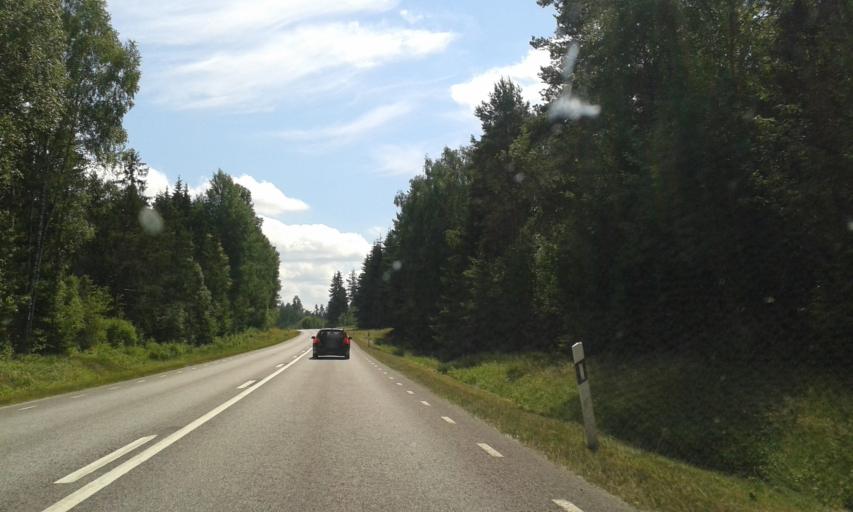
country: SE
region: Joenkoeping
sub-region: Varnamo Kommun
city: Rydaholm
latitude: 56.9797
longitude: 14.3062
